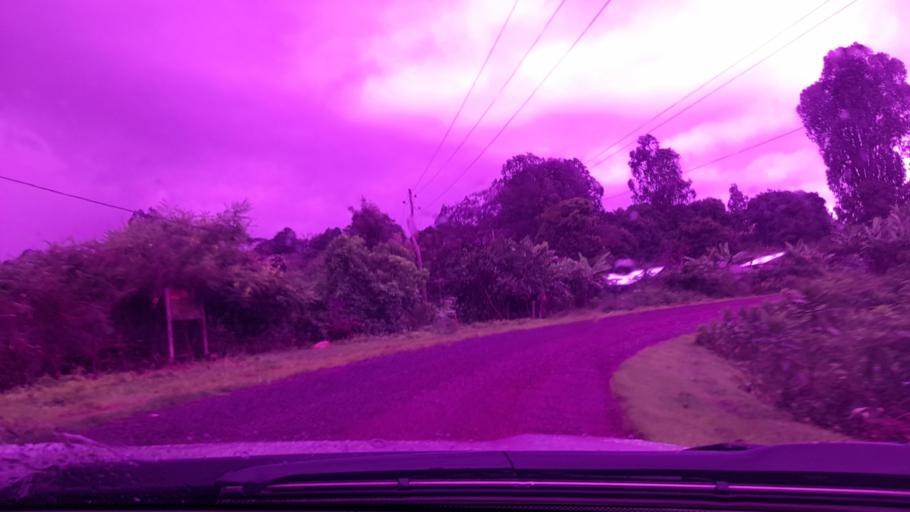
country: ET
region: Oromiya
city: Metu
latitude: 8.4437
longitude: 35.6236
